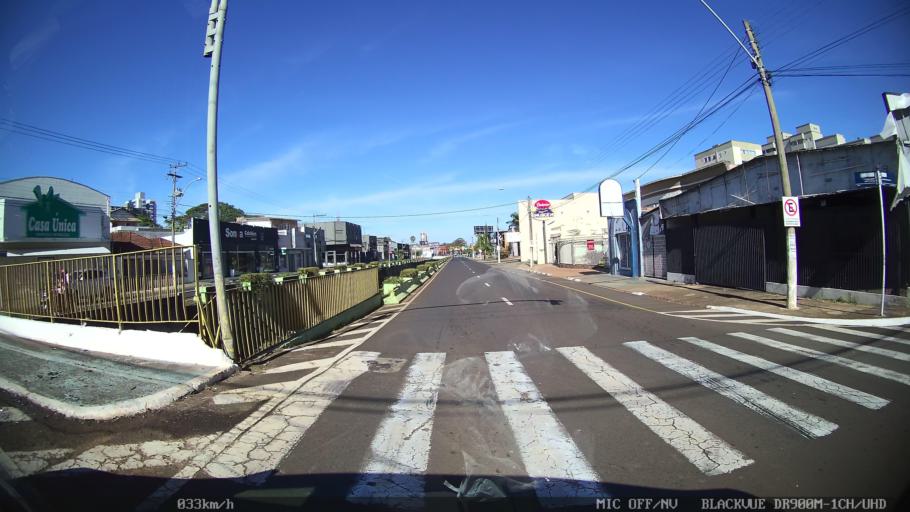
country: BR
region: Sao Paulo
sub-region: Franca
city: Franca
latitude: -20.5435
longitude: -47.3972
